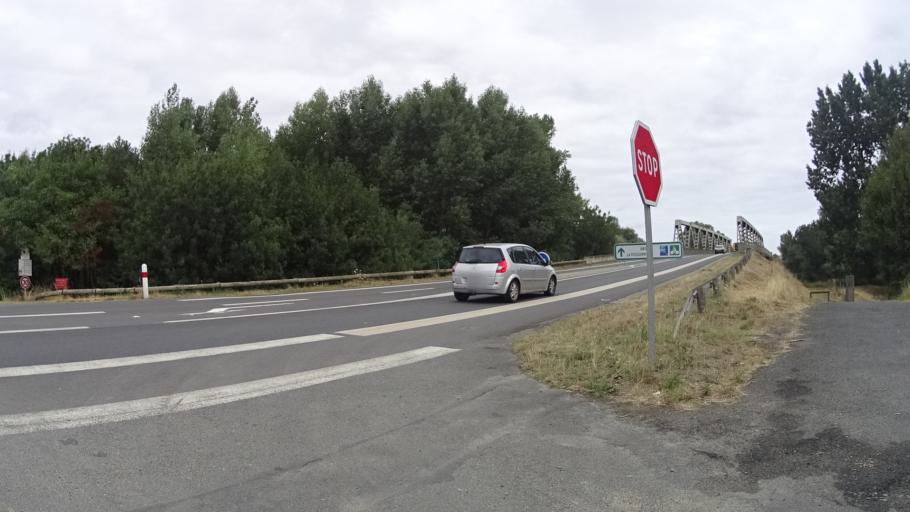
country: FR
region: Pays de la Loire
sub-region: Departement de Maine-et-Loire
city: Chalonnes-sur-Loire
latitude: 47.3626
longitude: -0.7572
